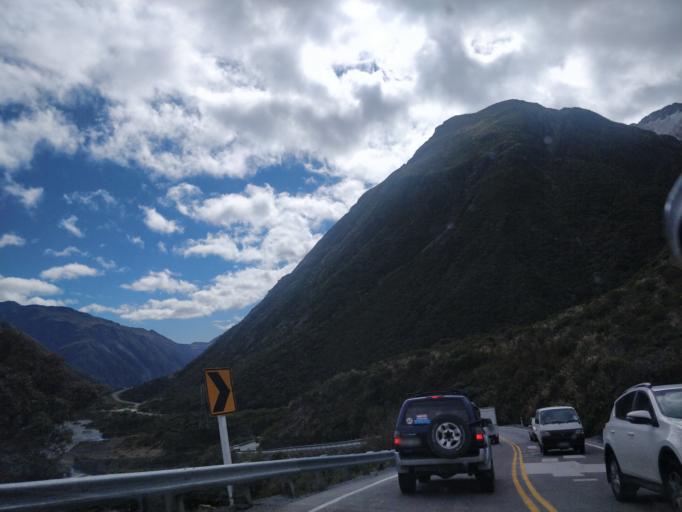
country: NZ
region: West Coast
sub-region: Grey District
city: Greymouth
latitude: -42.8975
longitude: 171.5586
